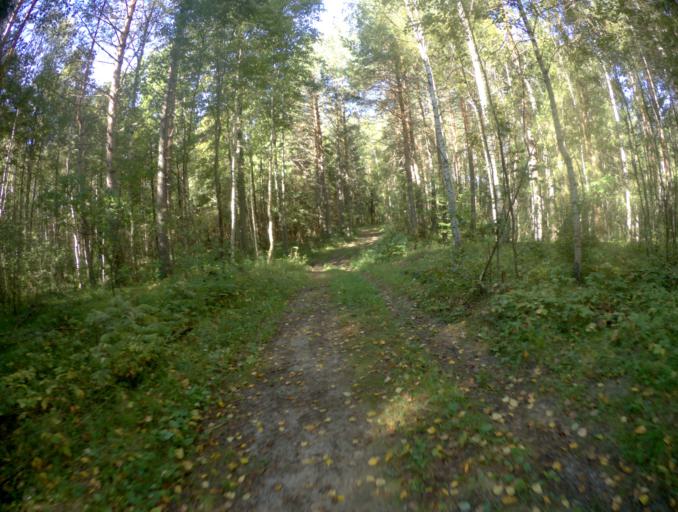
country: RU
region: Vladimir
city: Nikologory
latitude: 56.1088
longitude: 41.9074
